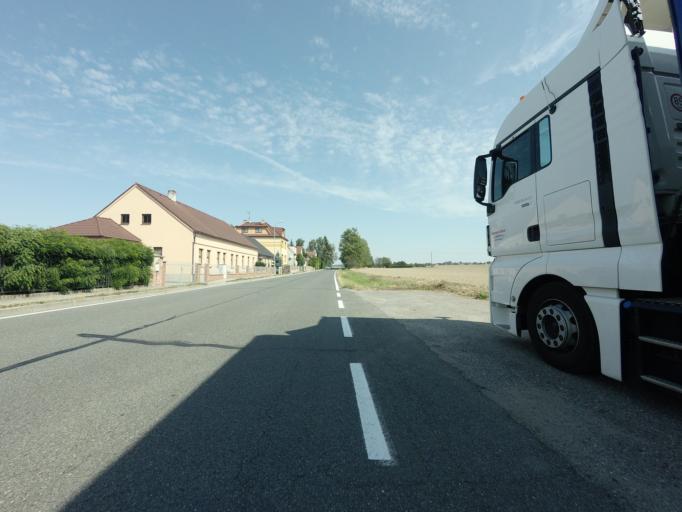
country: CZ
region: Jihocesky
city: Bernartice
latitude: 49.3716
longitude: 14.3794
